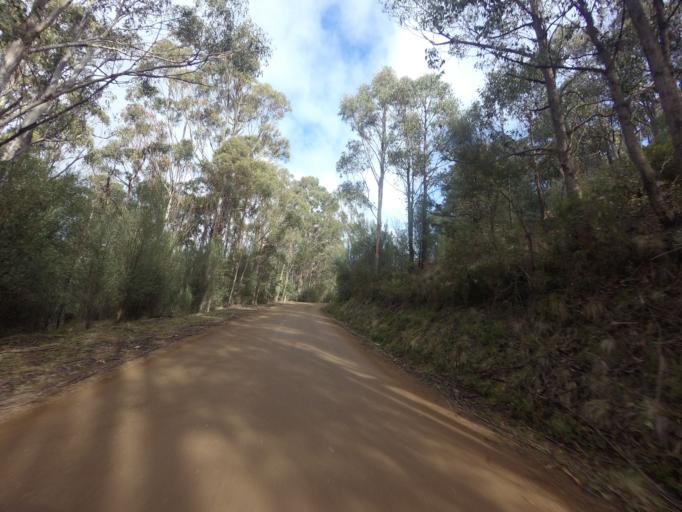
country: AU
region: Tasmania
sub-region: Derwent Valley
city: New Norfolk
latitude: -42.7893
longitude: 146.9336
